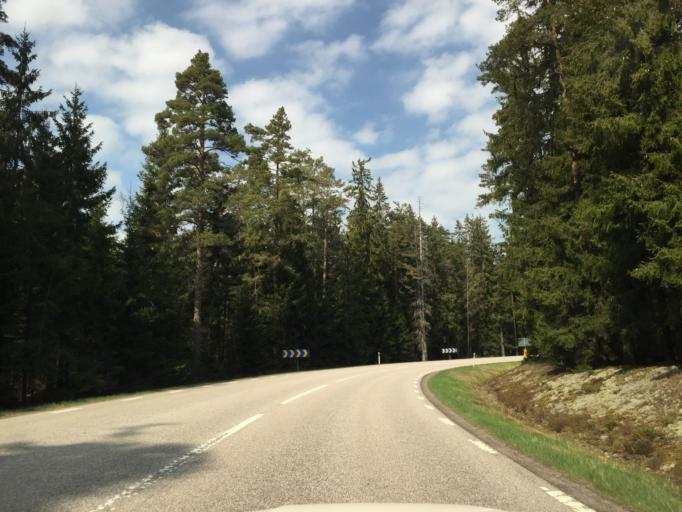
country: SE
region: Vaestra Goetaland
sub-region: Bengtsfors Kommun
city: Dals Langed
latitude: 58.8234
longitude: 12.1375
